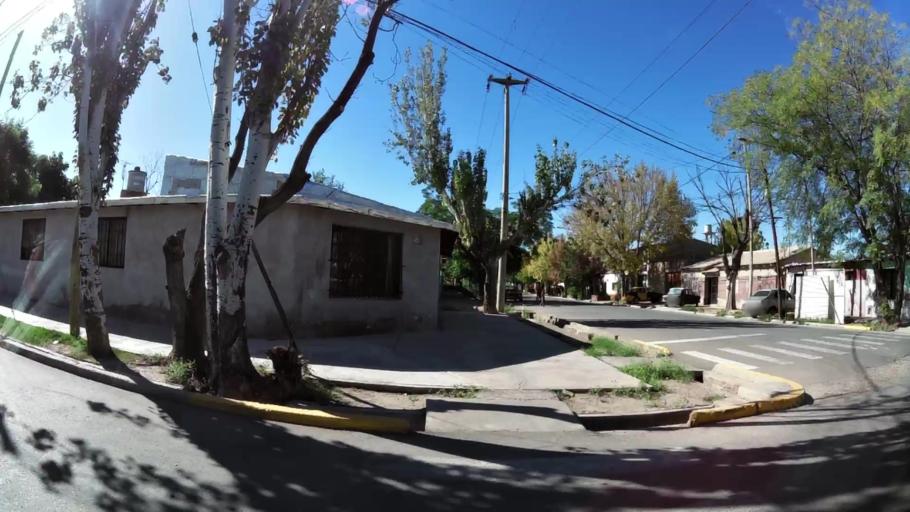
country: AR
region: Mendoza
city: Las Heras
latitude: -32.8409
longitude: -68.8209
